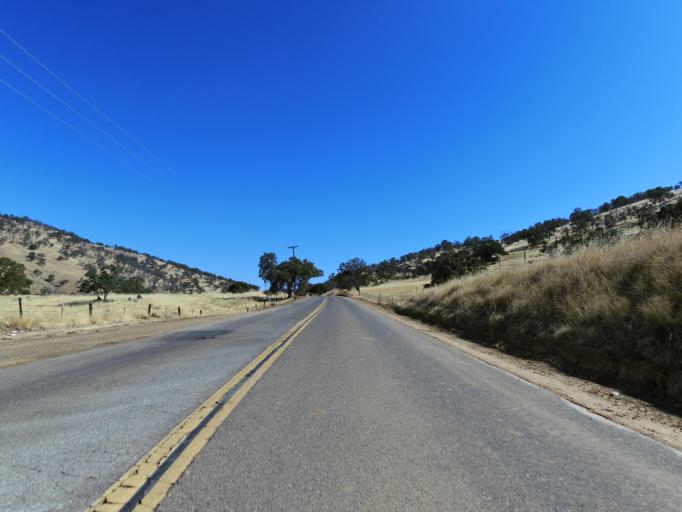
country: US
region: California
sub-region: Merced County
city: Planada
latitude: 37.6203
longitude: -120.3088
